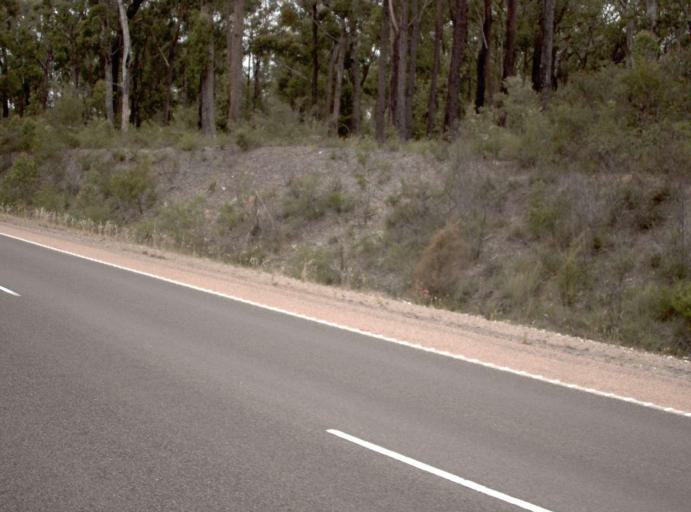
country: AU
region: Victoria
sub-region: East Gippsland
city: Lakes Entrance
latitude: -37.6964
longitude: 147.9957
